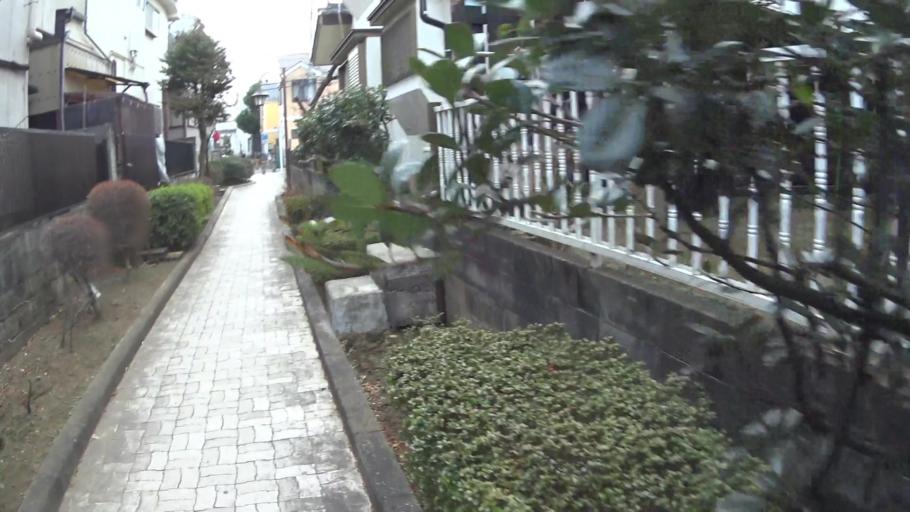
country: JP
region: Tokyo
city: Mitaka-shi
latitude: 35.6756
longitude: 139.5861
